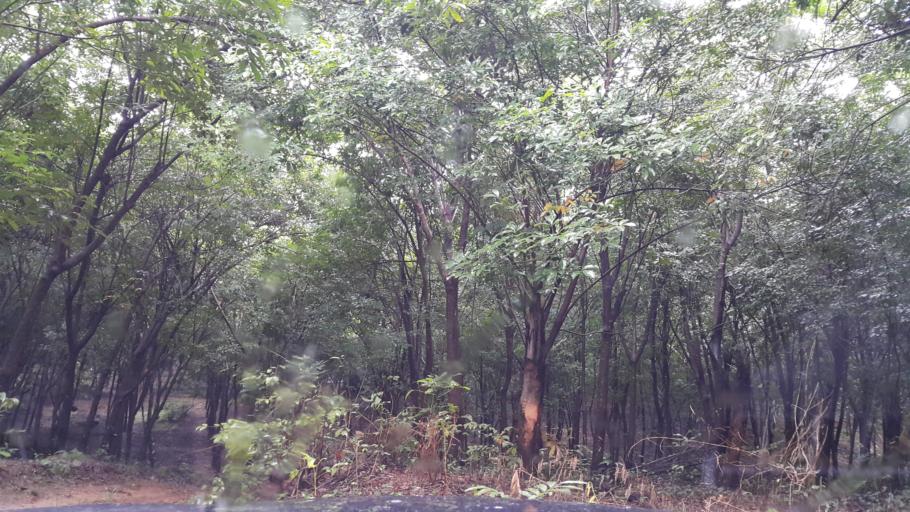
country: TH
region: Phayao
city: Phu Sang
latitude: 19.5965
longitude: 100.3993
